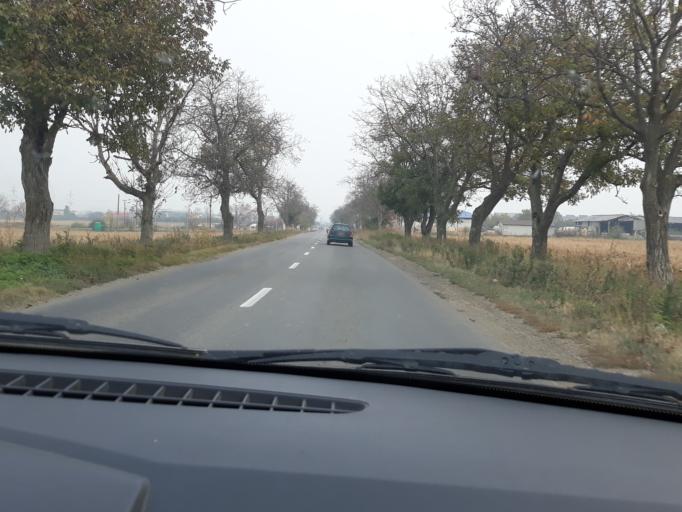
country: RO
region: Bihor
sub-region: Comuna Santandrei
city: Santandrei
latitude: 47.0519
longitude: 21.8768
